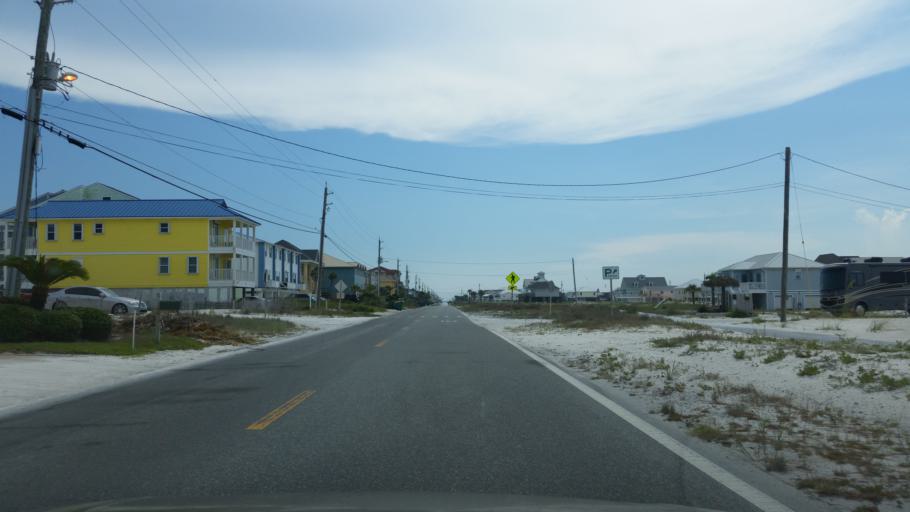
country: US
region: Florida
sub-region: Santa Rosa County
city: Navarre
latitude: 30.3751
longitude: -86.8989
